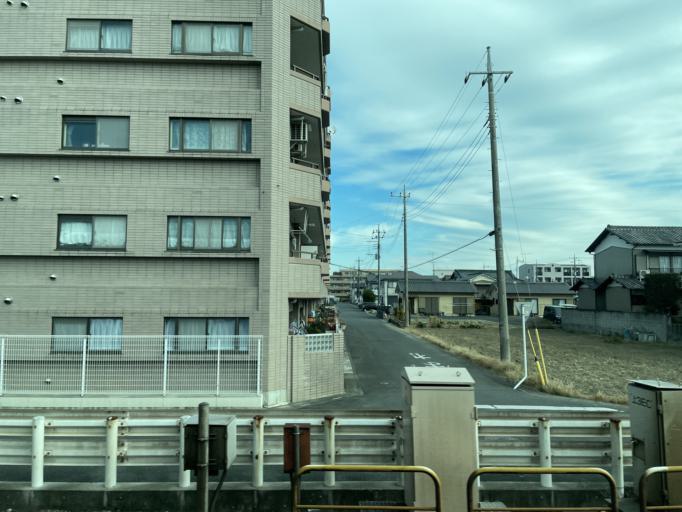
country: JP
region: Saitama
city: Fukiage-fujimi
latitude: 36.1171
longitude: 139.4290
